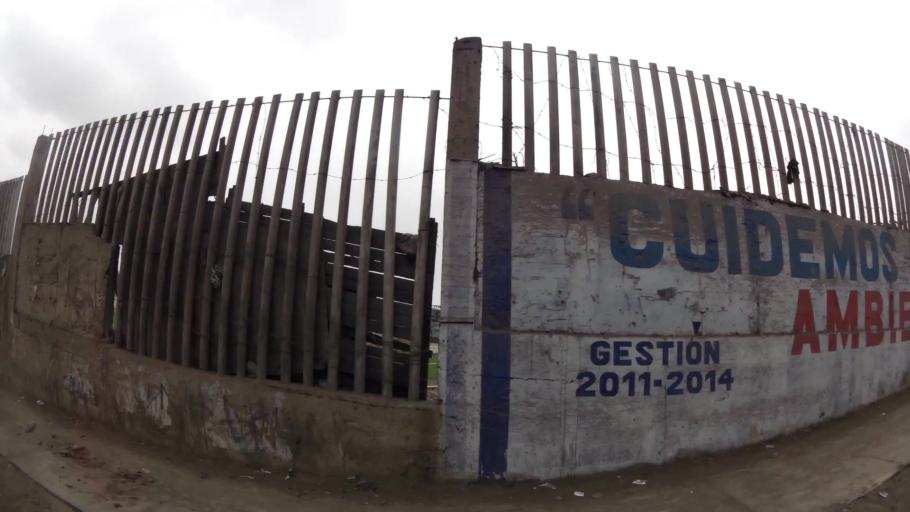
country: PE
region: Lima
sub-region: Lima
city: Surco
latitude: -12.1482
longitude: -76.9650
